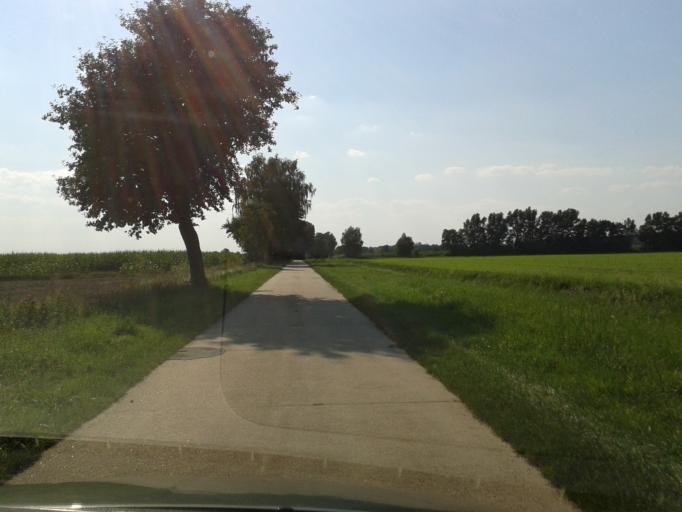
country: DE
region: Lower Saxony
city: Lubbow
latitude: 52.9080
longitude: 11.2097
